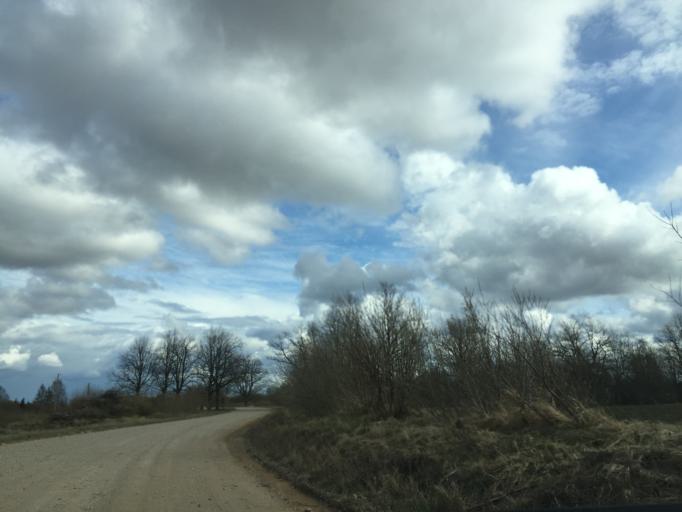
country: LV
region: Limbazu Rajons
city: Limbazi
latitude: 57.6172
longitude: 24.7165
